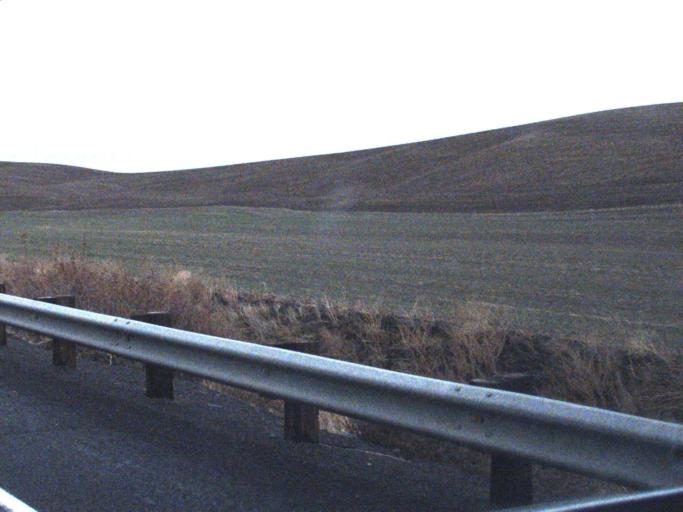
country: US
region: Washington
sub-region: Walla Walla County
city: Waitsburg
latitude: 46.2083
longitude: -118.1376
